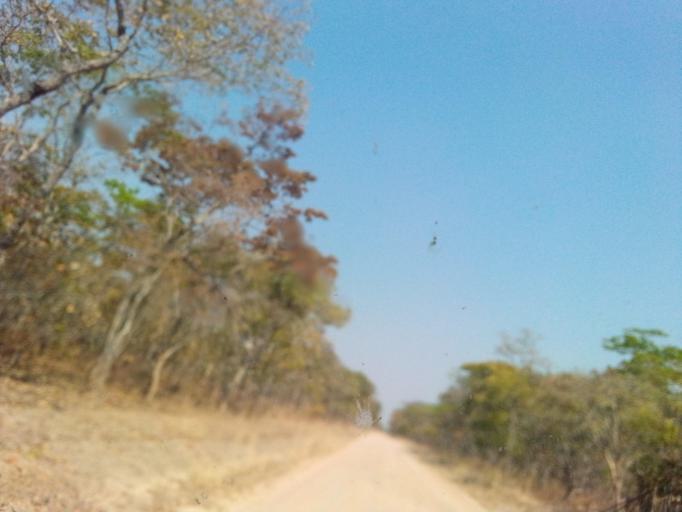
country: ZM
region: Northern
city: Mpika
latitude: -12.2285
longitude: 30.9129
